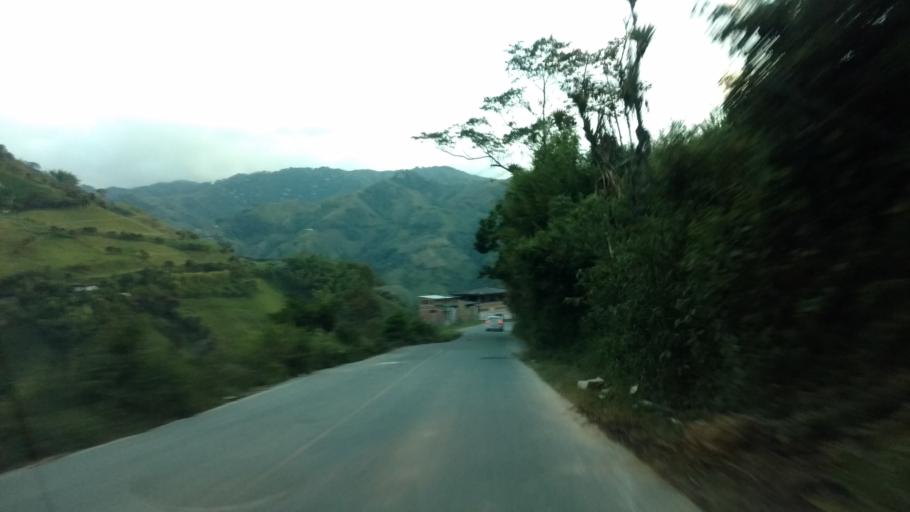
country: CO
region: Caldas
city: Aranzazu
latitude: 5.2660
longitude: -75.4968
